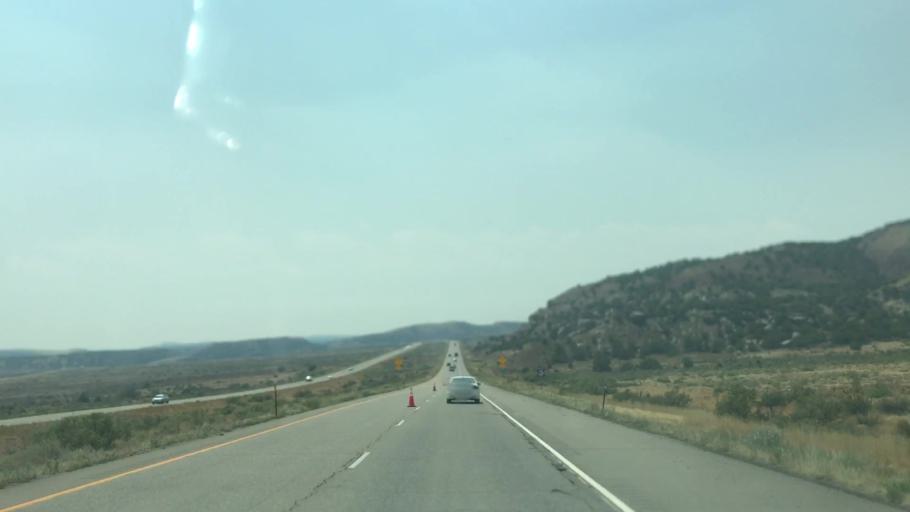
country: US
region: Colorado
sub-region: Garfield County
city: Parachute
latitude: 39.3903
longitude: -108.1335
